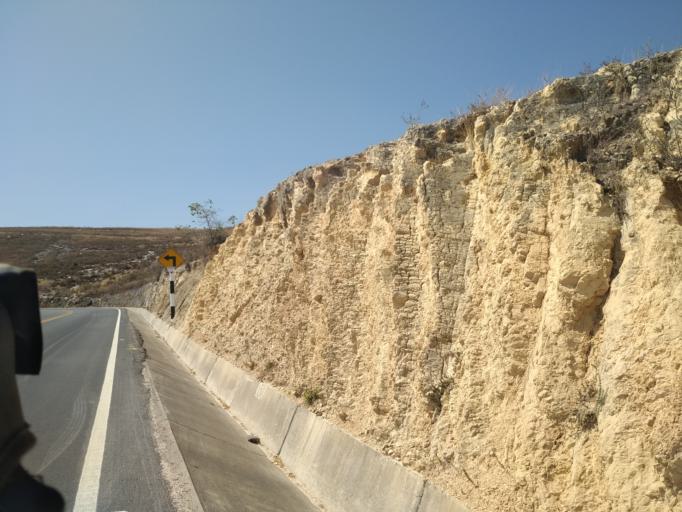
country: PE
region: Cajamarca
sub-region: Provincia de Cajamarca
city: Llacanora
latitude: -7.2063
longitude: -78.3907
